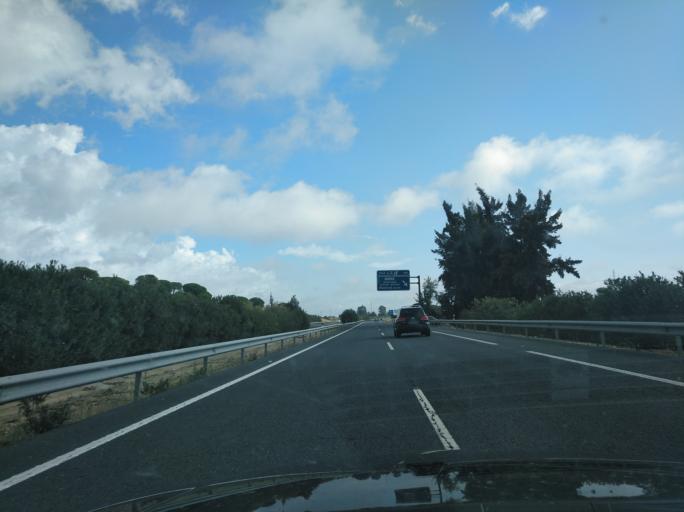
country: ES
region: Andalusia
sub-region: Provincia de Huelva
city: Cartaya
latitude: 37.3226
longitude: -7.0832
